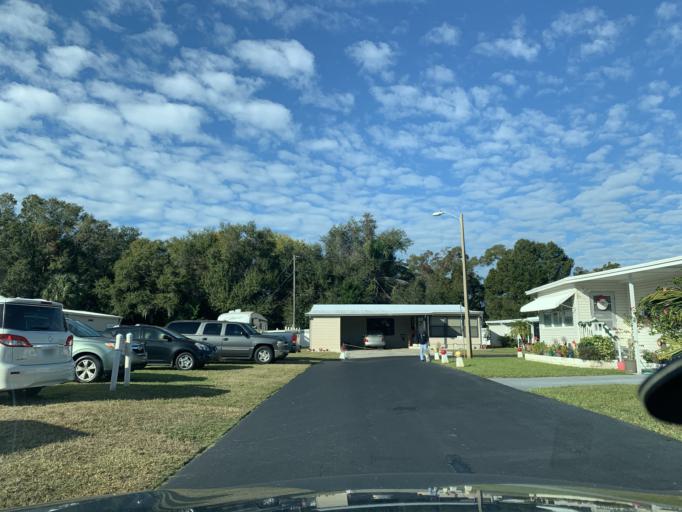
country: US
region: Florida
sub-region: Pinellas County
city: Kenneth City
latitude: 27.8175
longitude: -82.7470
